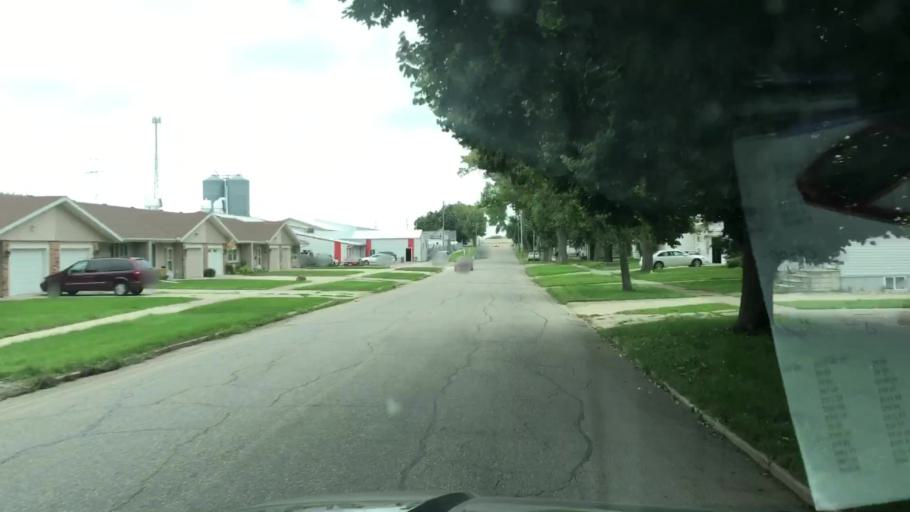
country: US
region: Iowa
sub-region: O'Brien County
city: Sheldon
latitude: 43.1775
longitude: -95.8506
